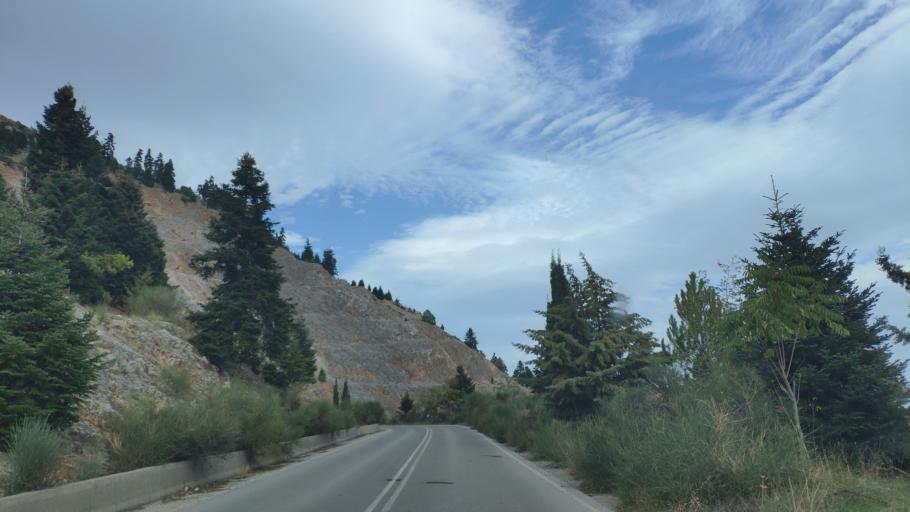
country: GR
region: Central Greece
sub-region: Nomos Fokidos
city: Amfissa
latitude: 38.6522
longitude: 22.3827
